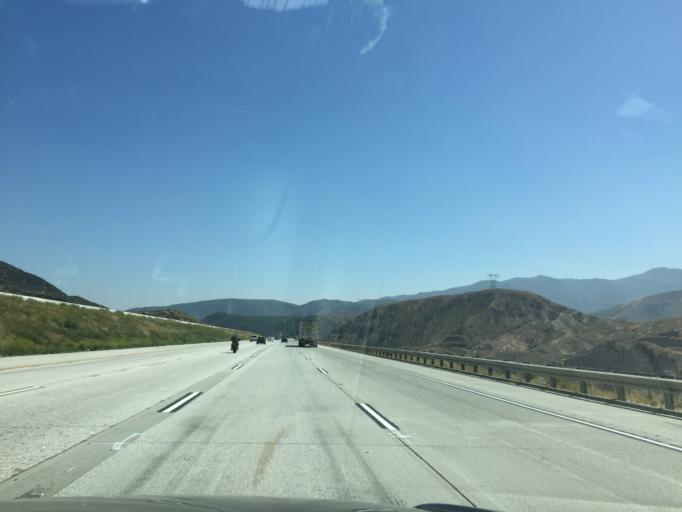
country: US
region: California
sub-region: San Bernardino County
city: Oak Hills
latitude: 34.2866
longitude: -117.4520
